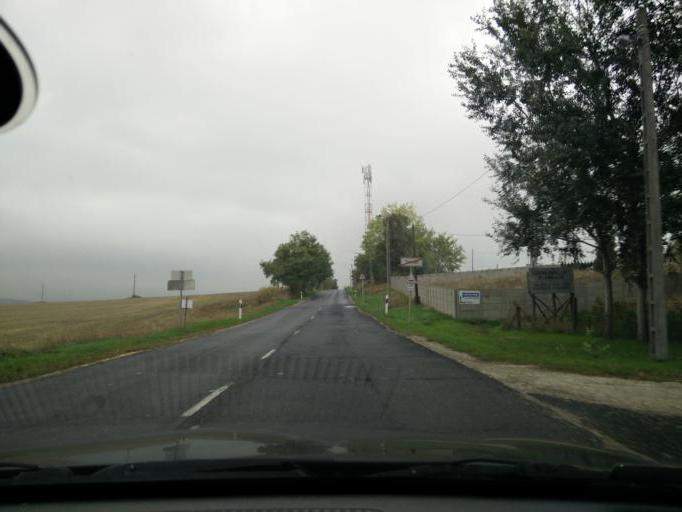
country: HU
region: Komarom-Esztergom
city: Tarjan
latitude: 47.6139
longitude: 18.5119
